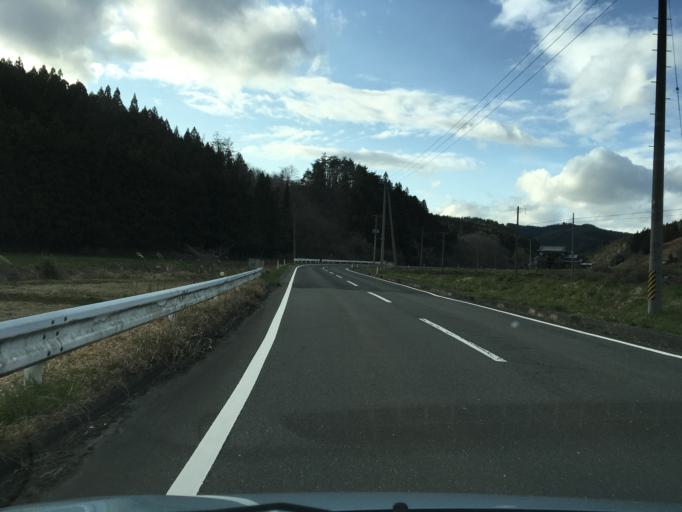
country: JP
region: Iwate
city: Ichinoseki
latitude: 38.7958
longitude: 141.3201
